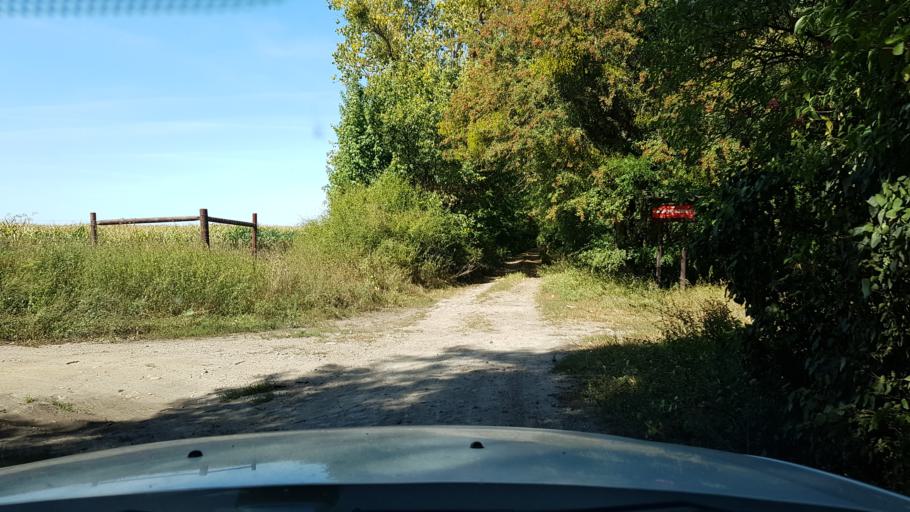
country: PL
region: West Pomeranian Voivodeship
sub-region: Powiat gryfinski
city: Cedynia
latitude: 52.8528
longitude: 14.2270
